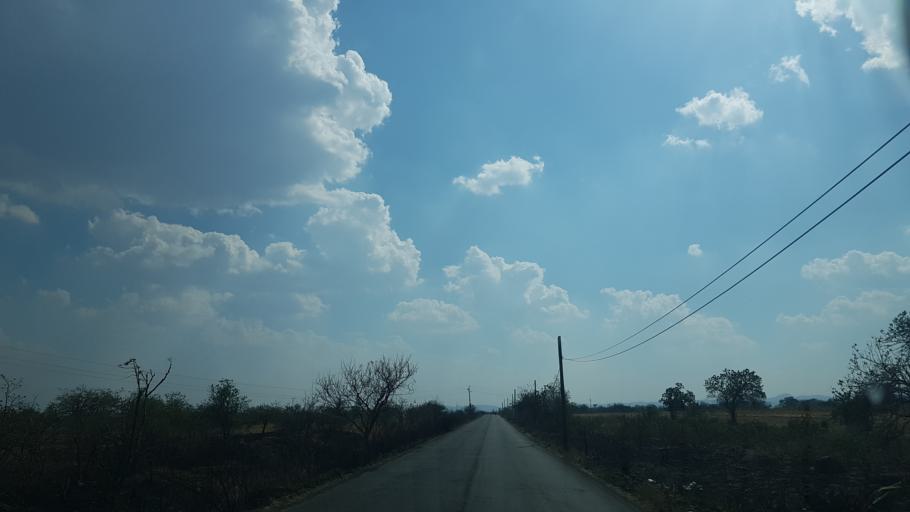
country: MX
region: Puebla
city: Atlixco
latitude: 18.9061
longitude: -98.4808
